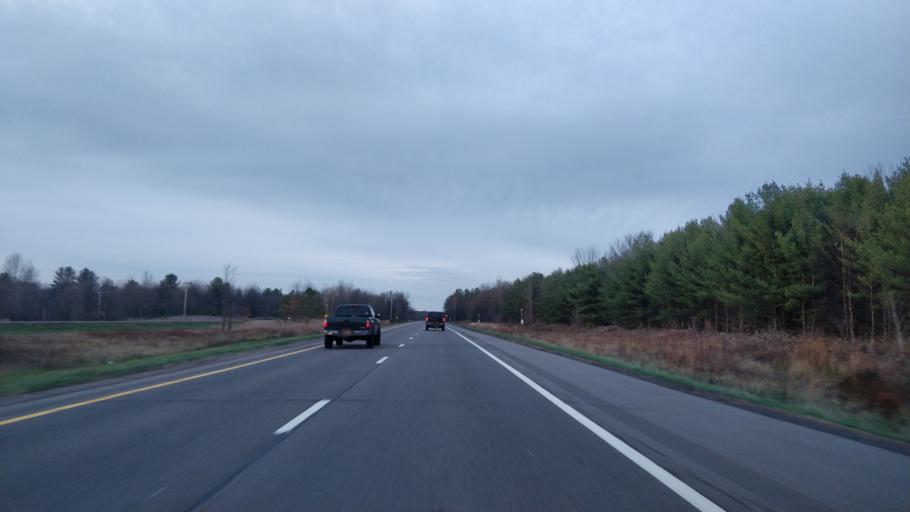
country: US
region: New York
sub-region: Oswego County
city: Central Square
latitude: 43.3348
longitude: -76.1224
